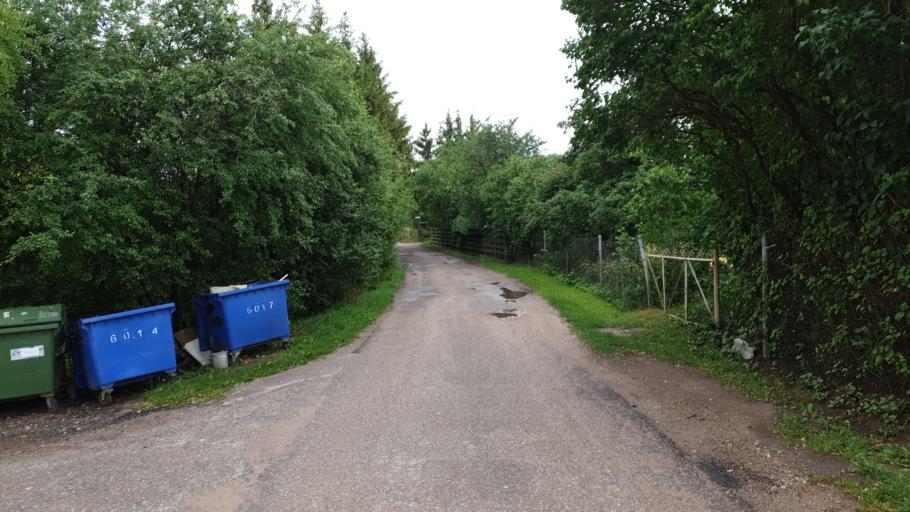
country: LT
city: Grigiskes
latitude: 54.7678
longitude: 25.0143
